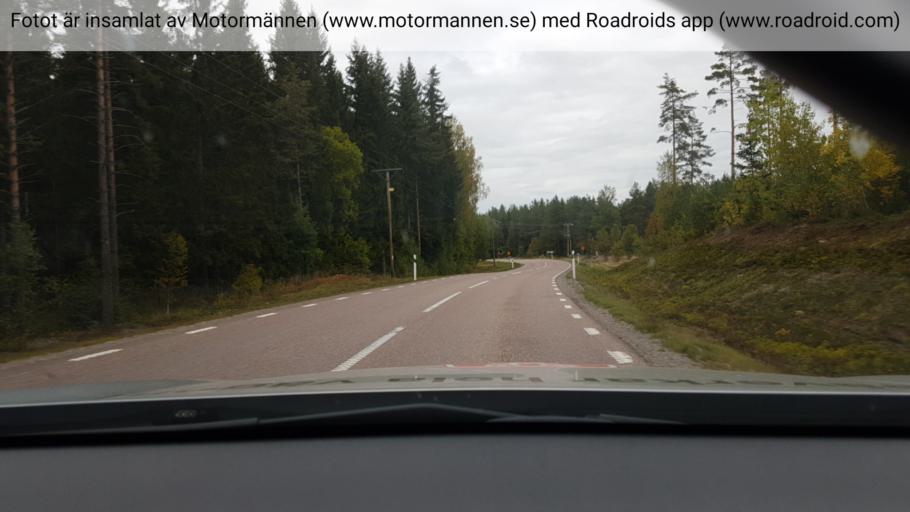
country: SE
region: Gaevleborg
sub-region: Gavle Kommun
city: Hedesunda
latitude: 60.4928
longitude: 16.9371
